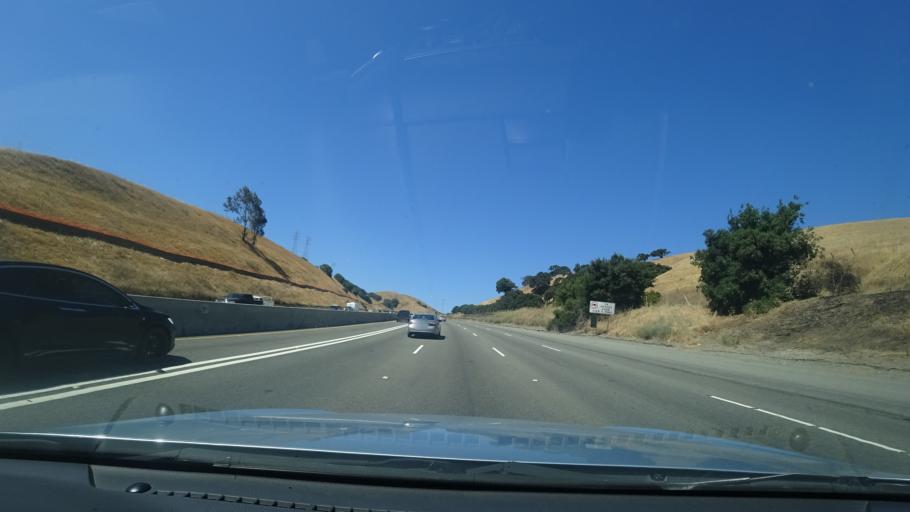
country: US
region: California
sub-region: Alameda County
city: Fremont
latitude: 37.5651
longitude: -121.9019
